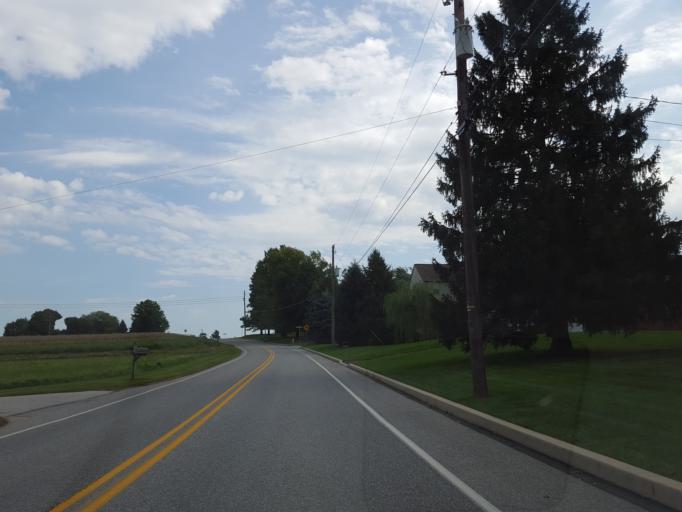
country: US
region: Pennsylvania
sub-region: York County
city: Spry
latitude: 39.9168
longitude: -76.6754
